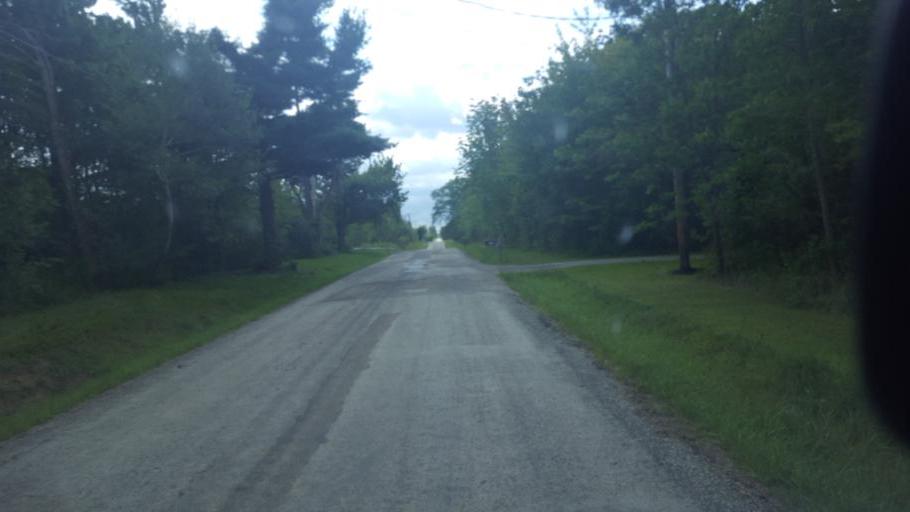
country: US
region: Ohio
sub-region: Geauga County
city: Chardon
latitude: 41.6545
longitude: -81.1127
